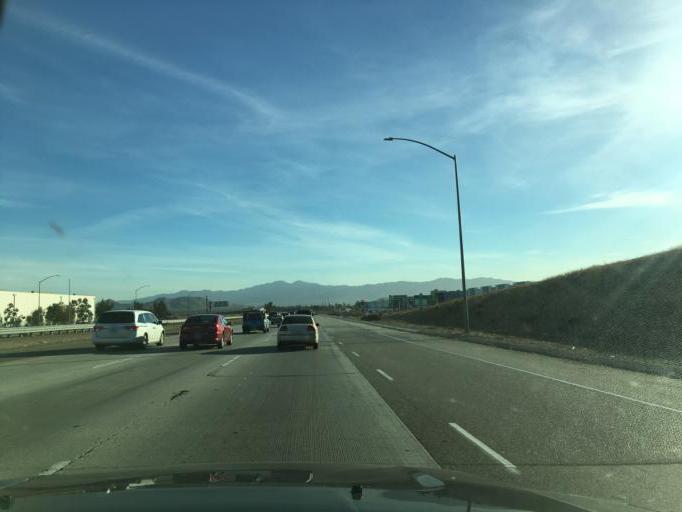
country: US
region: California
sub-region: Riverside County
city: Mira Loma
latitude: 34.0006
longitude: -117.5506
